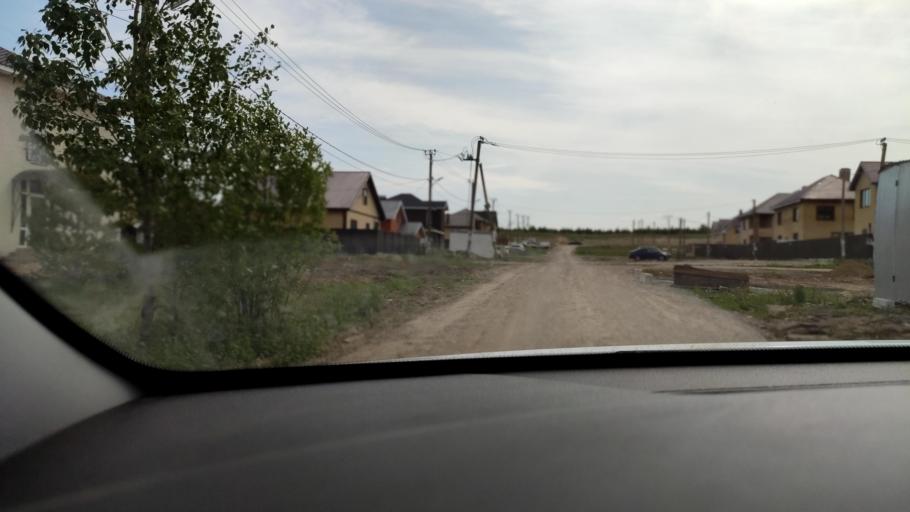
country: RU
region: Tatarstan
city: Vysokaya Gora
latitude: 55.7906
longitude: 49.2630
